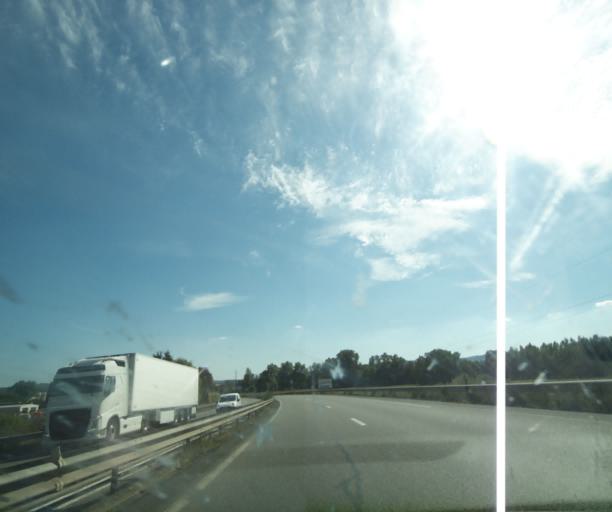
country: FR
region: Limousin
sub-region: Departement de la Correze
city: Saint-Pantaleon-de-Larche
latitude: 45.1621
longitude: 1.4791
